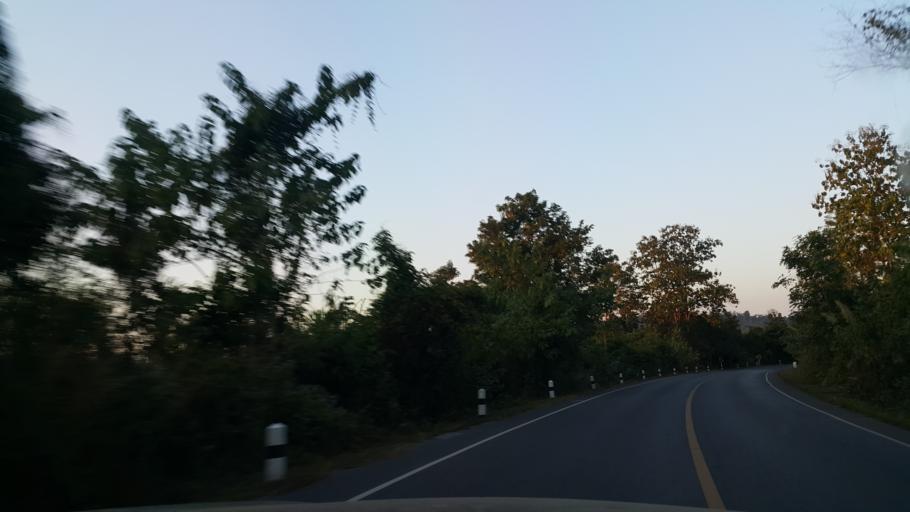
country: TH
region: Phrae
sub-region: Amphoe Wang Chin
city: Wang Chin
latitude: 17.8383
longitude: 99.6410
